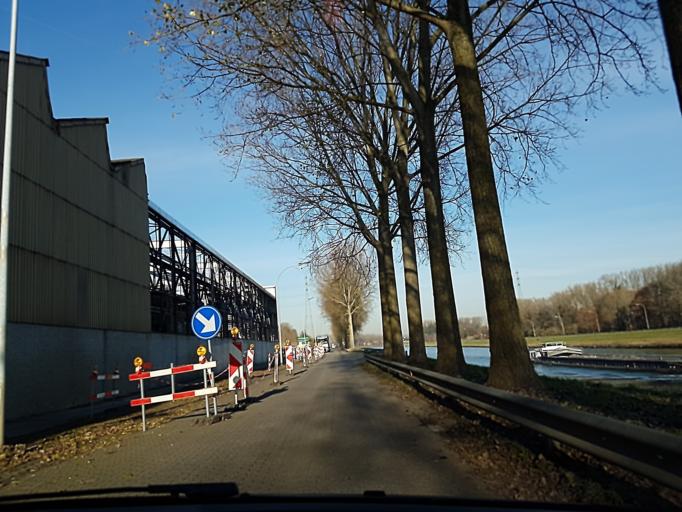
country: BE
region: Flanders
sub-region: Provincie Vlaams-Brabant
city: Kapelle-op-den-Bos
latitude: 51.0221
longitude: 4.3597
